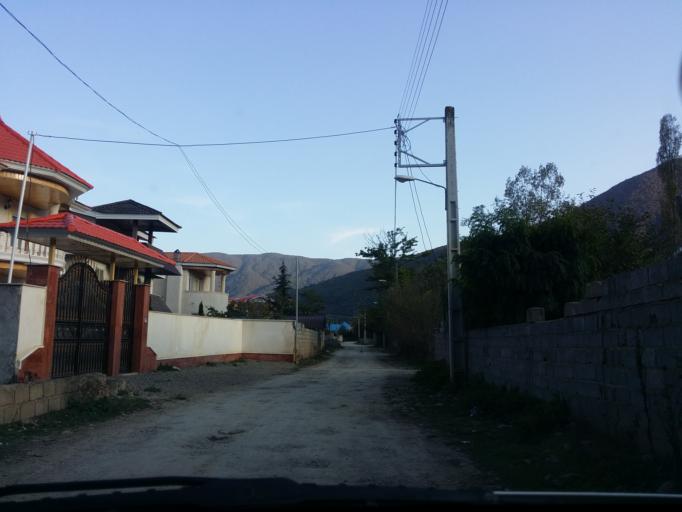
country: IR
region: Mazandaran
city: `Abbasabad
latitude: 36.5116
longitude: 51.1834
